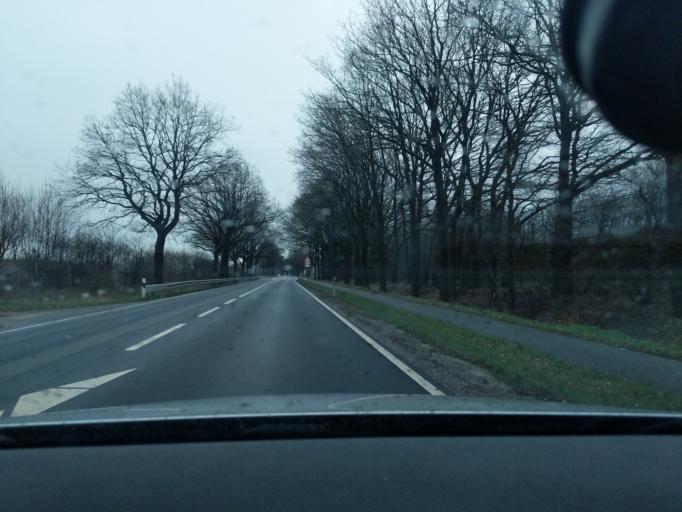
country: DE
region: Lower Saxony
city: Dudenbuttel
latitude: 53.5729
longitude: 9.3925
